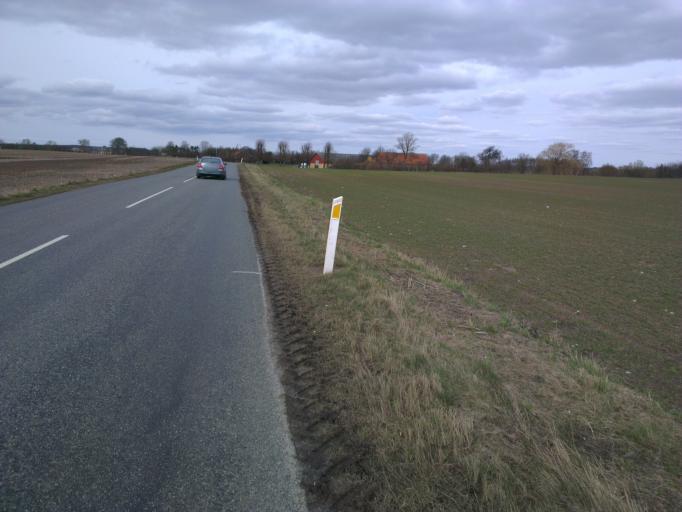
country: DK
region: Capital Region
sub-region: Frederikssund Kommune
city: Frederikssund
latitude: 55.8034
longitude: 12.0217
